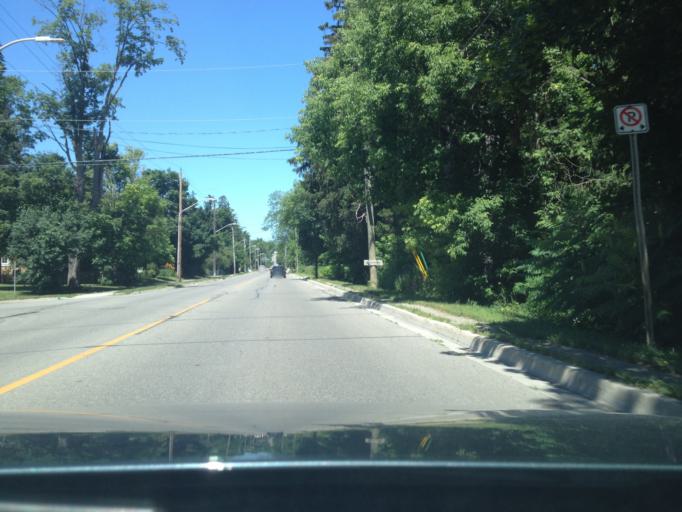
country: CA
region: Ontario
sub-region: Halton
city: Milton
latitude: 43.6641
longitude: -79.9218
